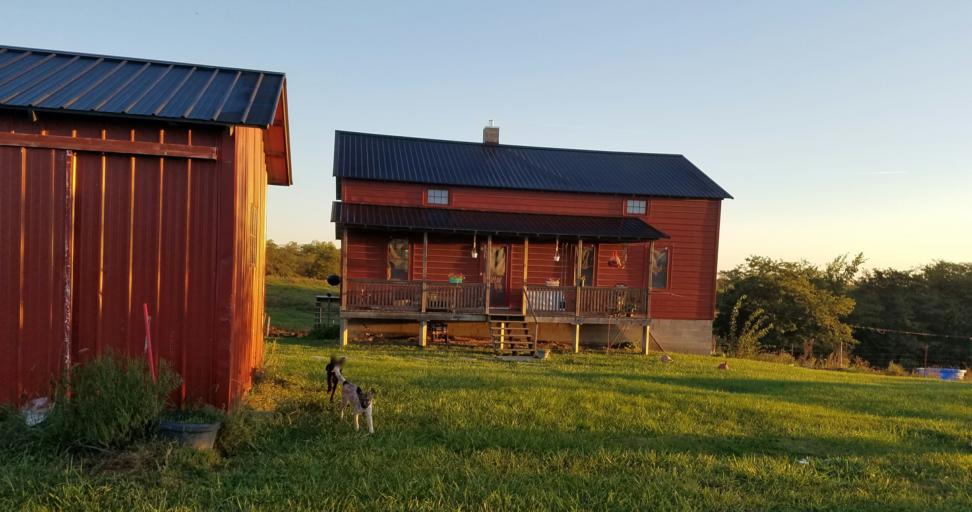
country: US
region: Iowa
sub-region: Decatur County
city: Lamoni
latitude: 40.6379
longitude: -93.8880
